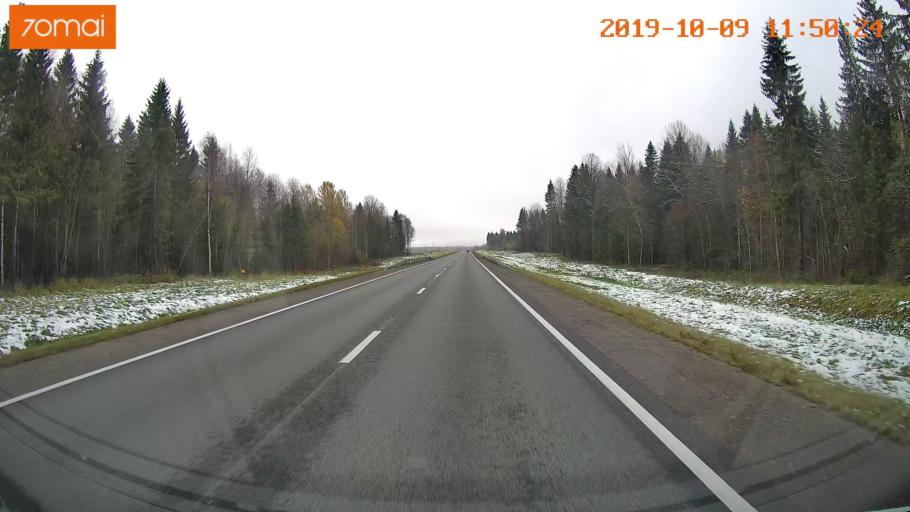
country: RU
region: Vologda
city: Gryazovets
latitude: 58.8060
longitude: 40.2458
